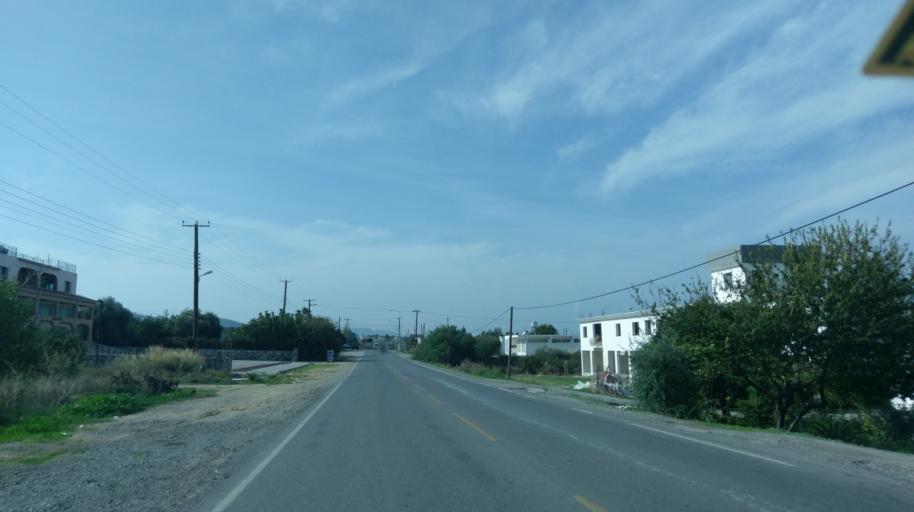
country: CY
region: Keryneia
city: Lapithos
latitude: 35.3513
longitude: 33.1373
